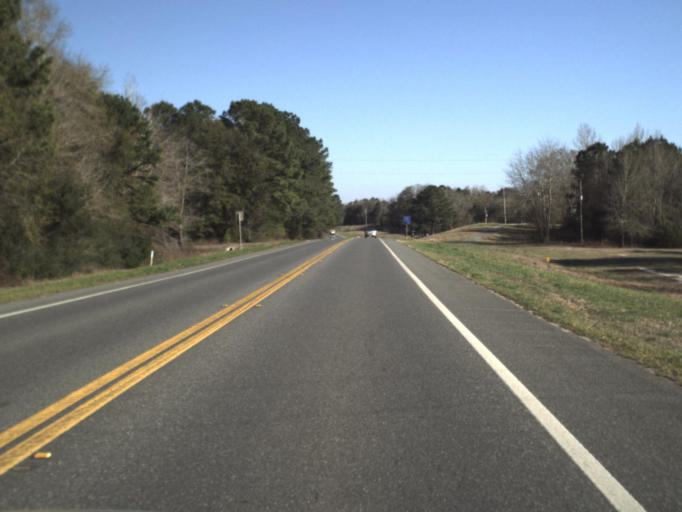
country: US
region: Florida
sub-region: Jackson County
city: Marianna
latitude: 30.7906
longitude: -85.3600
